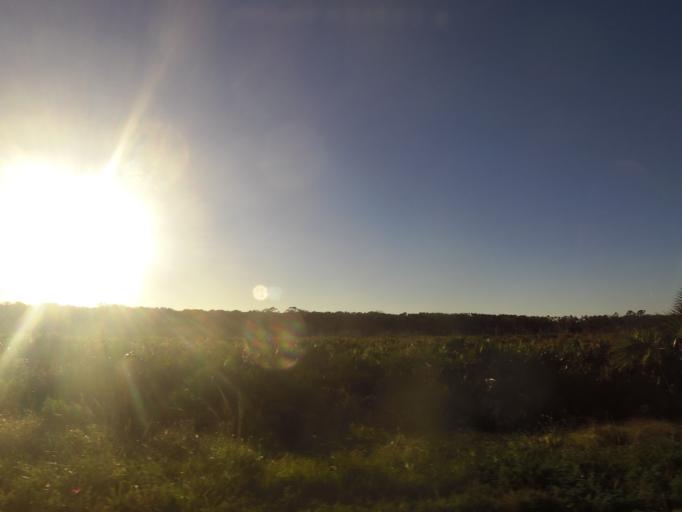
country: US
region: Florida
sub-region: Flagler County
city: Palm Coast
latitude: 29.6360
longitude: -81.2042
